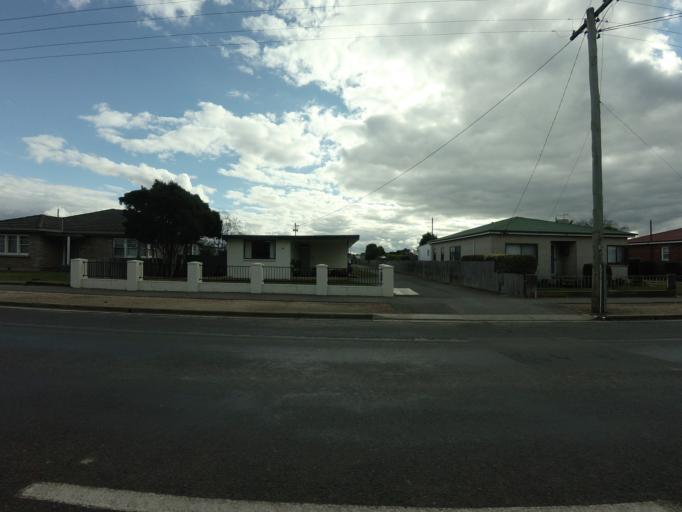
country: AU
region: Tasmania
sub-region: Northern Midlands
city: Longford
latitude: -41.6035
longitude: 147.1191
